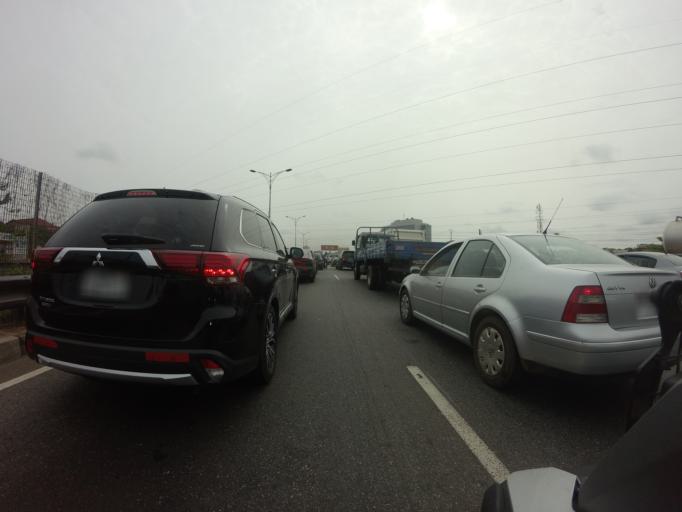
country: GH
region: Greater Accra
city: Dome
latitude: 5.6173
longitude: -0.1959
